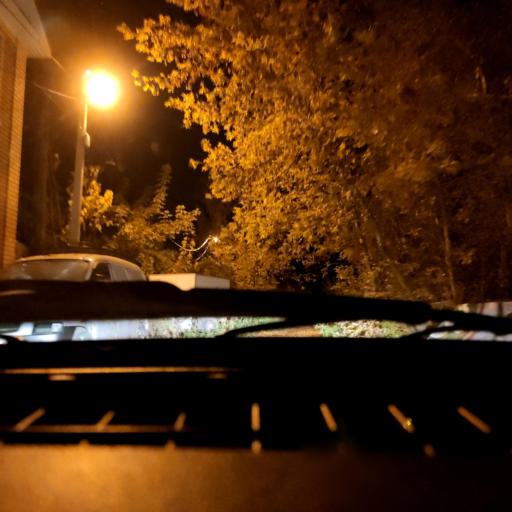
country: RU
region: Bashkortostan
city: Ufa
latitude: 54.7981
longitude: 56.1525
